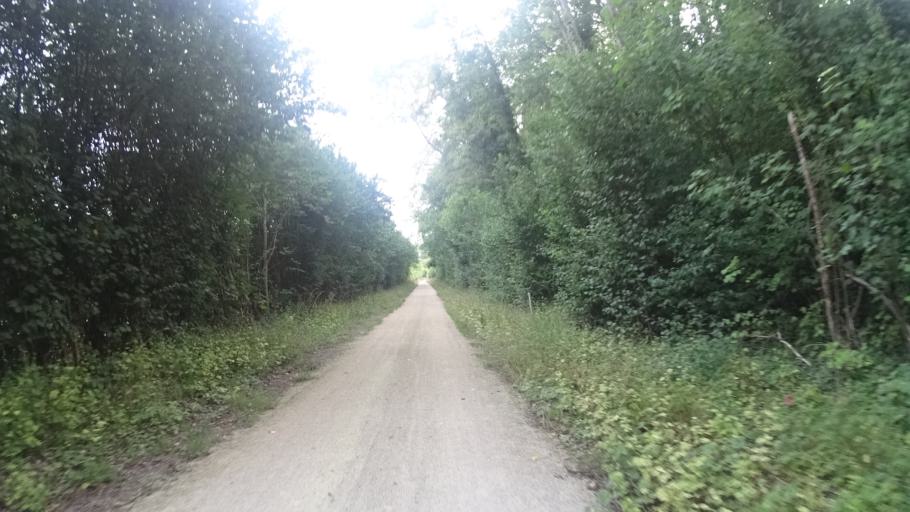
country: FR
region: Picardie
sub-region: Departement de l'Aisne
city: Origny-Sainte-Benoite
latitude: 49.8653
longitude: 3.5172
